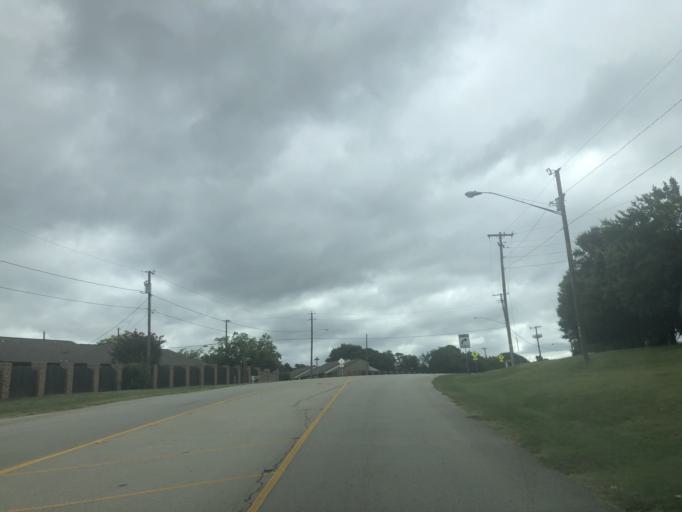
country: US
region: Texas
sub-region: Dallas County
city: Duncanville
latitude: 32.6663
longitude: -96.9534
